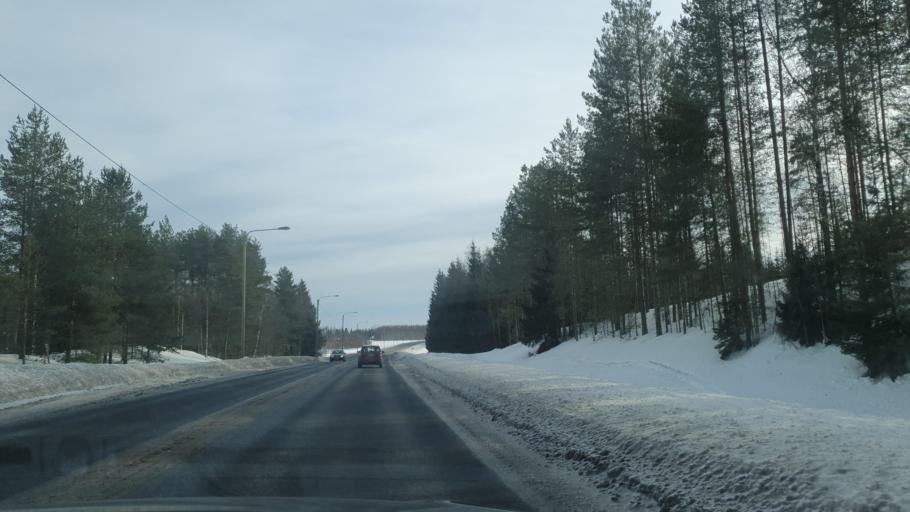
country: FI
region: Northern Ostrobothnia
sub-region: Oulu
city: Tyrnaevae
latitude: 64.9069
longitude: 25.7869
